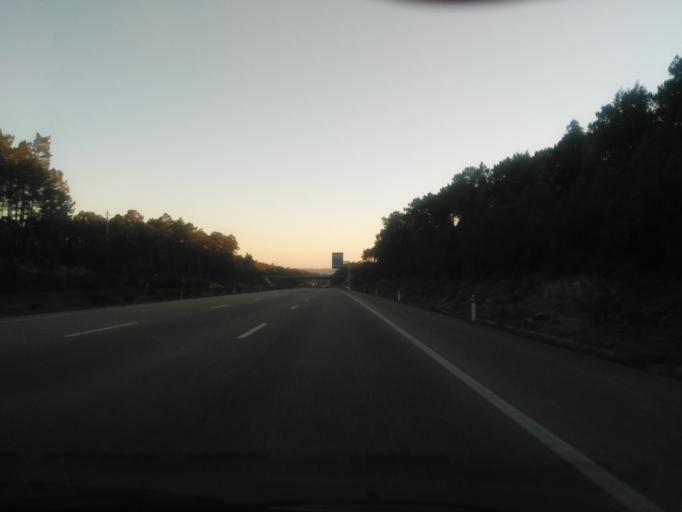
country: PT
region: Leiria
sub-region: Alcobaca
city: Pataias
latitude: 39.6596
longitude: -8.9589
